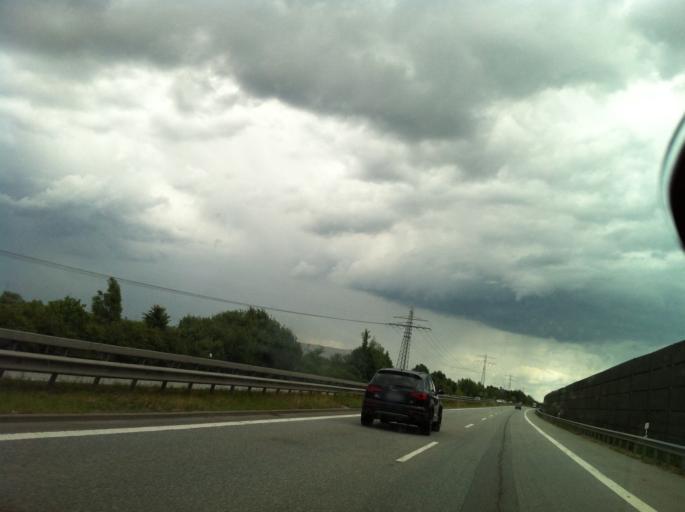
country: DE
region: Hamburg
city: Rothenburgsort
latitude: 53.5077
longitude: 10.0774
